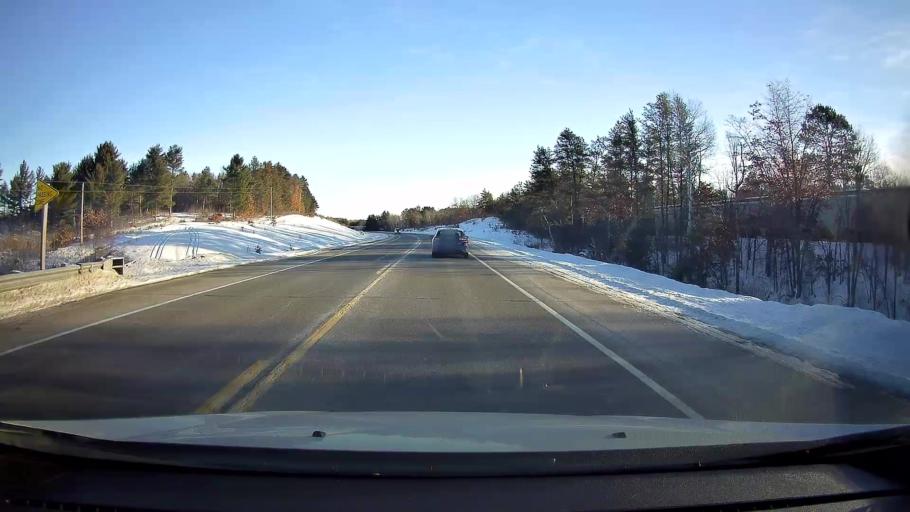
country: US
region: Wisconsin
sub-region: Washburn County
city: Spooner
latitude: 45.9215
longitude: -91.7299
